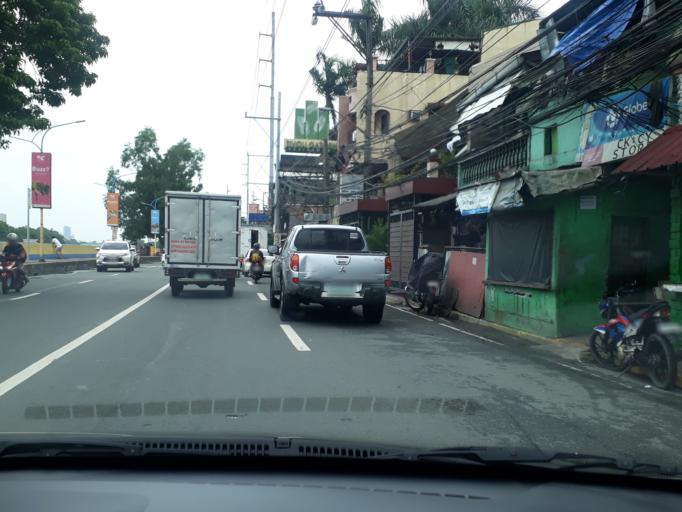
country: PH
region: Metro Manila
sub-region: Mandaluyong
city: Mandaluyong City
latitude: 14.5718
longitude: 121.0299
